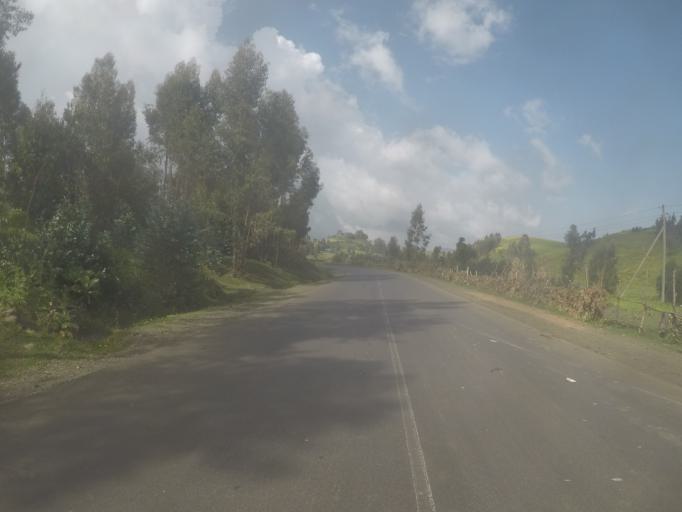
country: ET
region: Amhara
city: Gondar
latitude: 12.7714
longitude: 37.6309
